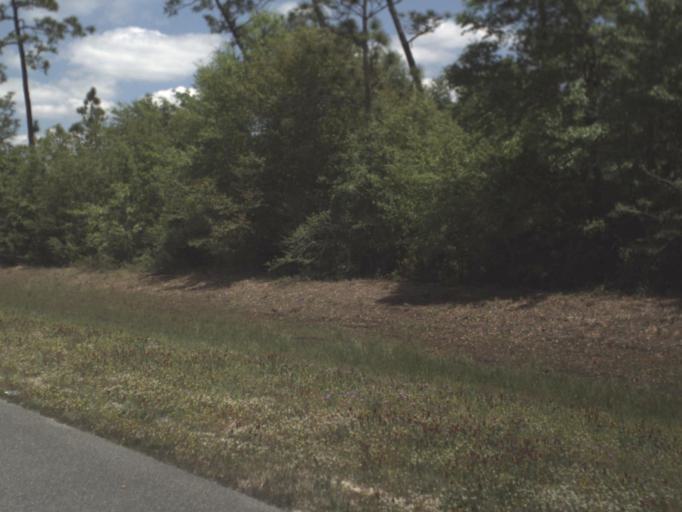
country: US
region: Florida
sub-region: Santa Rosa County
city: Point Baker
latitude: 30.7009
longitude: -87.0505
